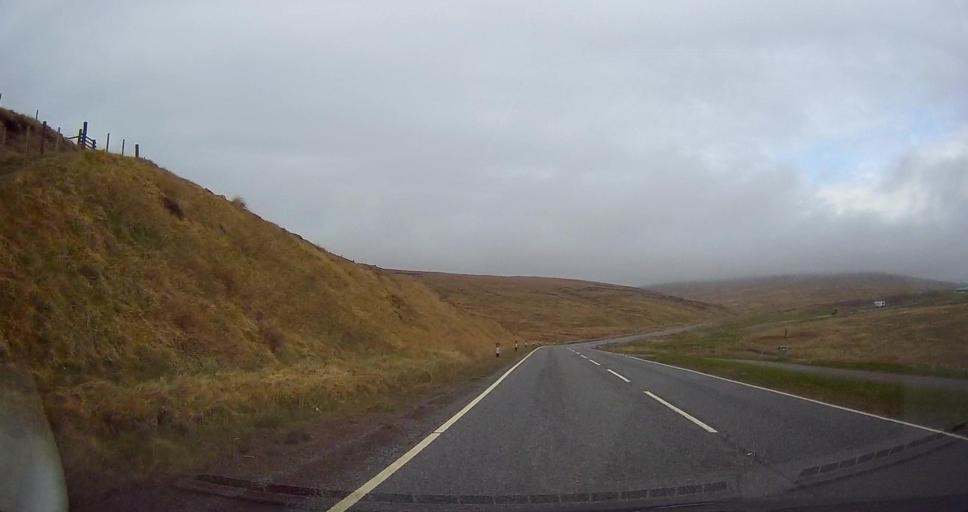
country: GB
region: Scotland
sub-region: Shetland Islands
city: Sandwick
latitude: 60.0011
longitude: -1.2796
